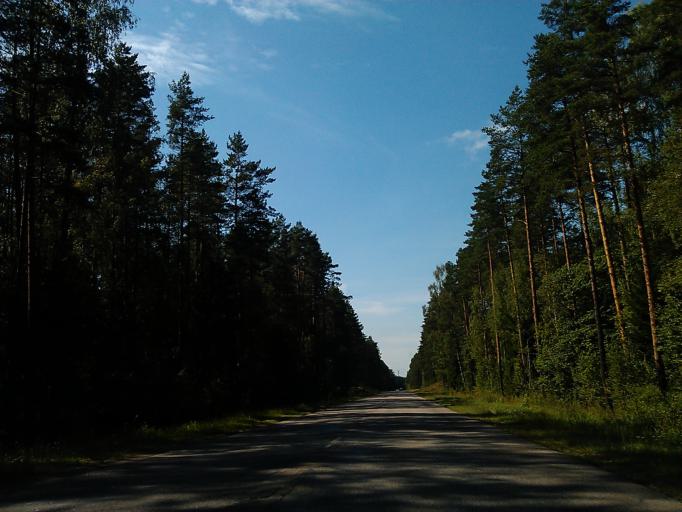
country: LV
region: Garkalne
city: Garkalne
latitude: 56.9432
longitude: 24.4270
